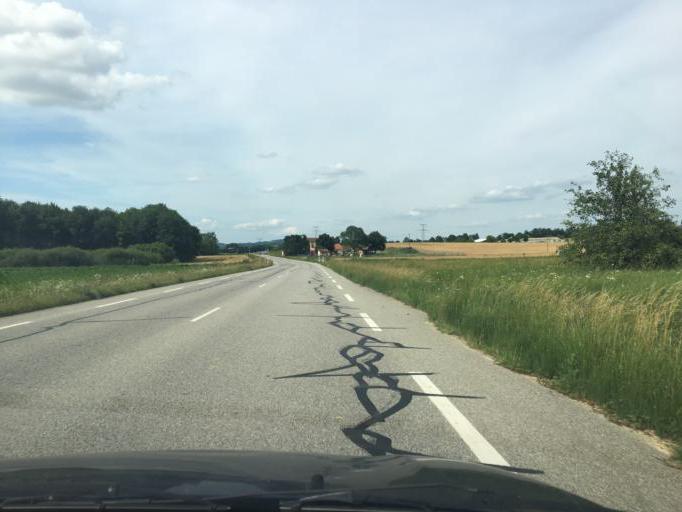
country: FR
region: Rhone-Alpes
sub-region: Departement de la Drome
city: Chanos-Curson
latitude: 45.0724
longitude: 4.9348
